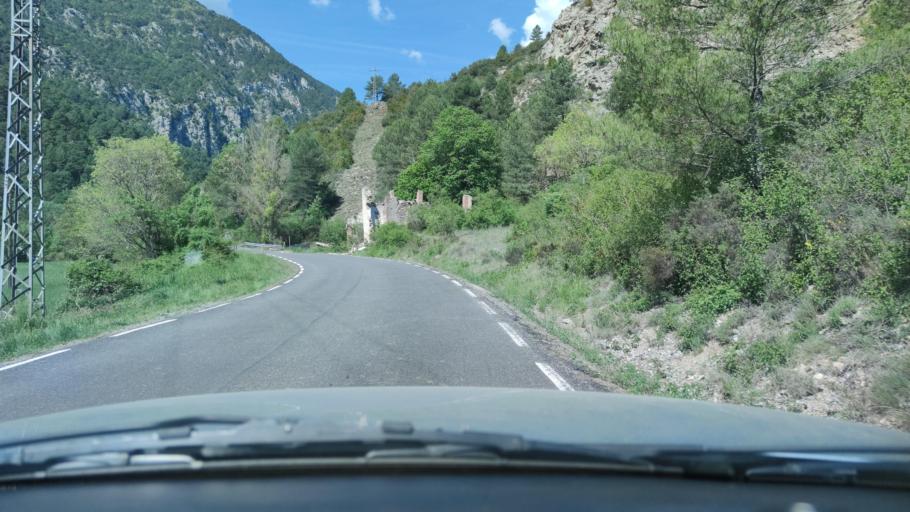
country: ES
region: Catalonia
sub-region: Provincia de Lleida
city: Coll de Nargo
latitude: 42.2914
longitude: 1.3332
